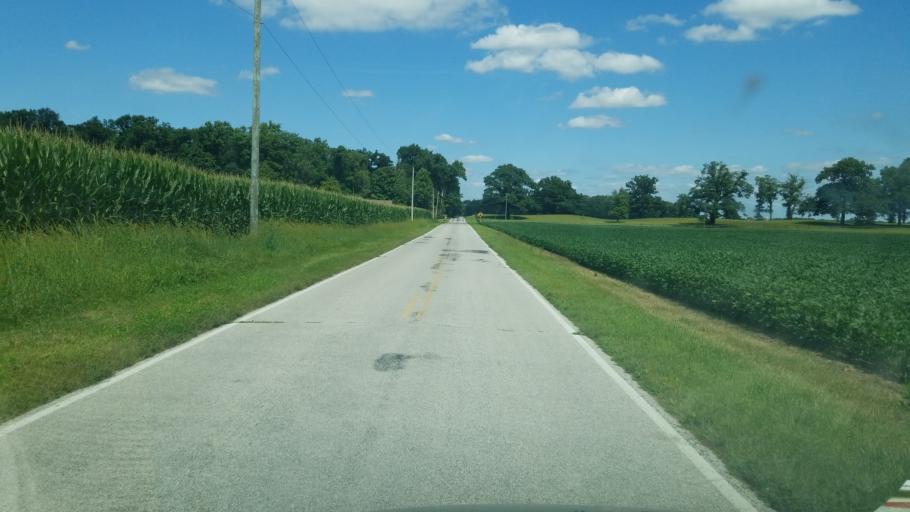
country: US
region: Ohio
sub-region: Fulton County
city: Delta
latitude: 41.6252
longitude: -84.0152
